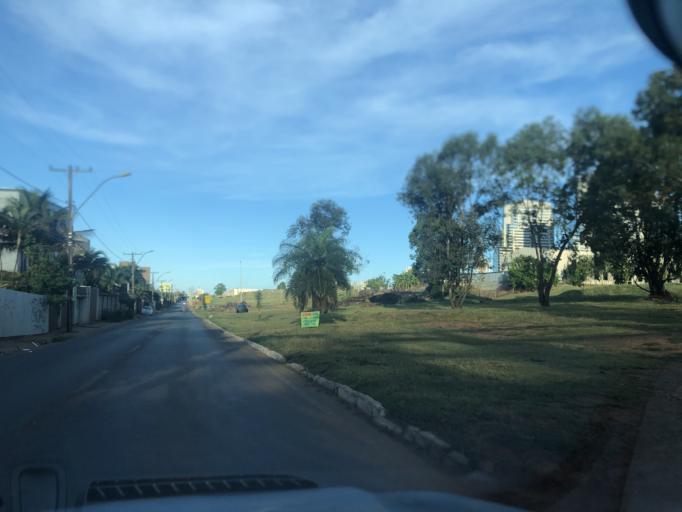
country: BR
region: Federal District
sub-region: Brasilia
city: Brasilia
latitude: -15.8291
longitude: -48.0459
